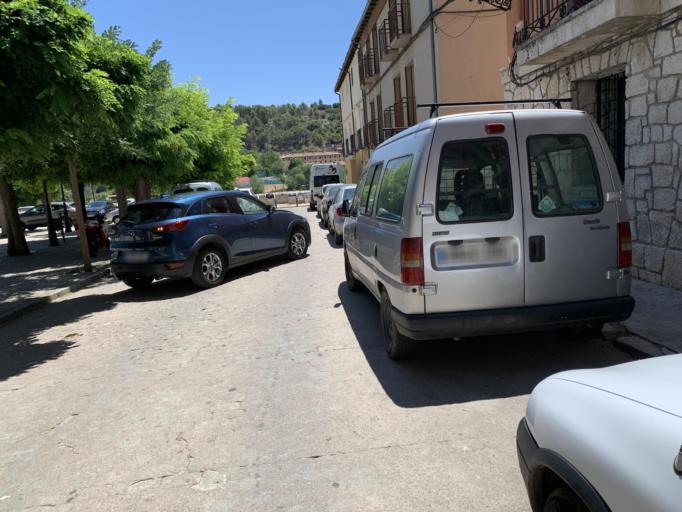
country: ES
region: Castille-La Mancha
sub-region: Provincia de Guadalajara
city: Pastrana
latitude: 40.4178
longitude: -2.9229
